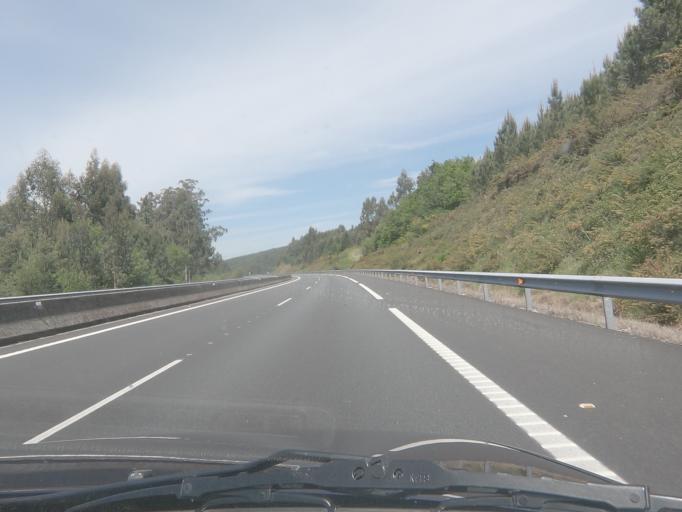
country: ES
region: Galicia
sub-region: Provincia de Pontevedra
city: Valga
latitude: 42.6952
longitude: -8.6355
